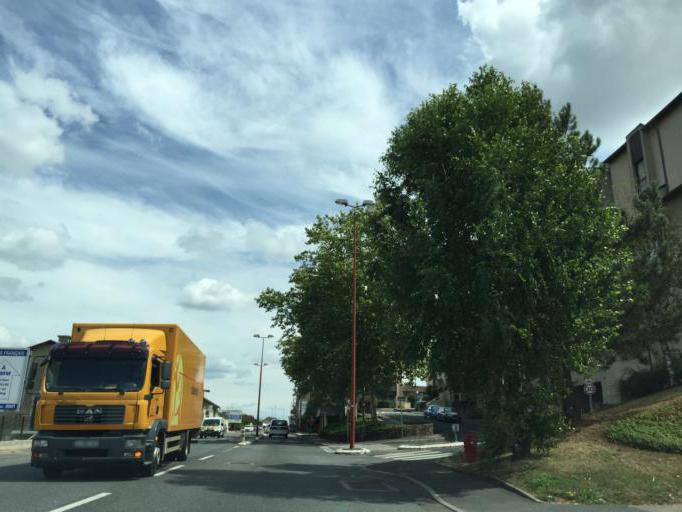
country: FR
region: Midi-Pyrenees
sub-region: Departement de l'Aveyron
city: Rodez
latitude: 44.3619
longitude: 2.5830
